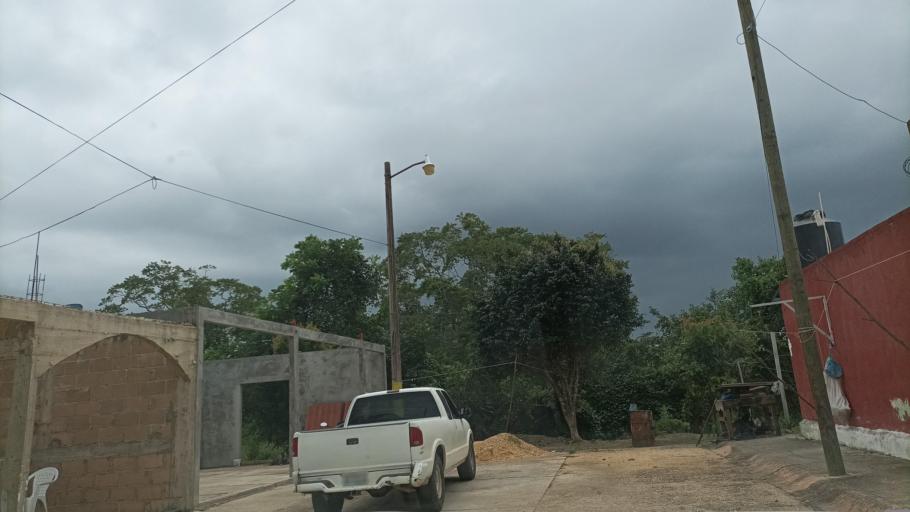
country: MX
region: Veracruz
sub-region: Soconusco
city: Fraccionamiento Santa Cruz
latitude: 17.9711
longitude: -94.8975
